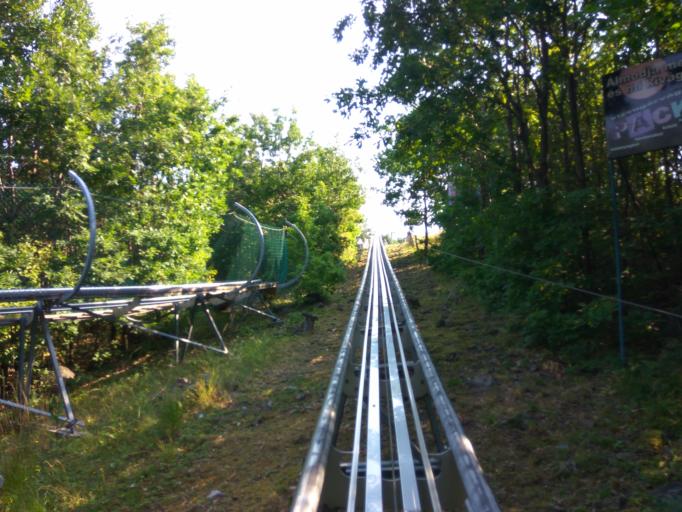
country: HU
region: Heves
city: Gyongyossolymos
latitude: 47.8485
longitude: 19.9650
